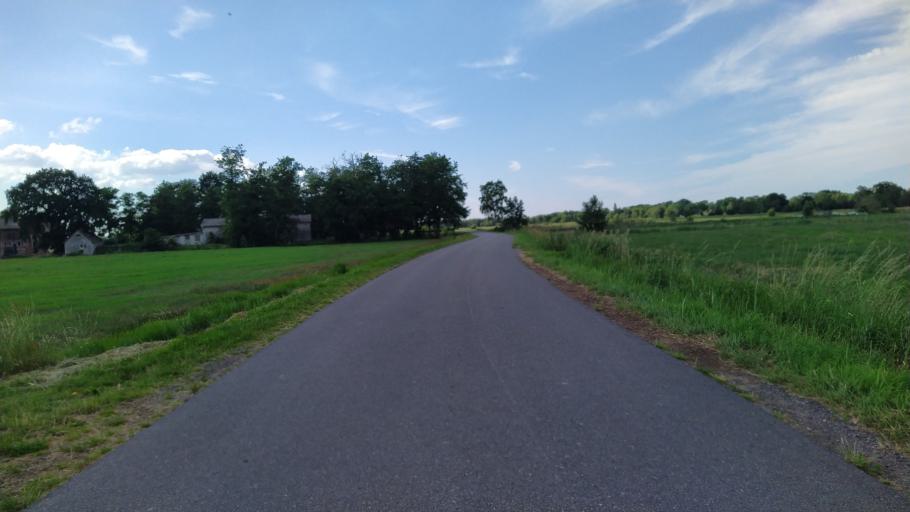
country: DE
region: Lower Saxony
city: Odisheim
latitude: 53.6637
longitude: 8.9298
